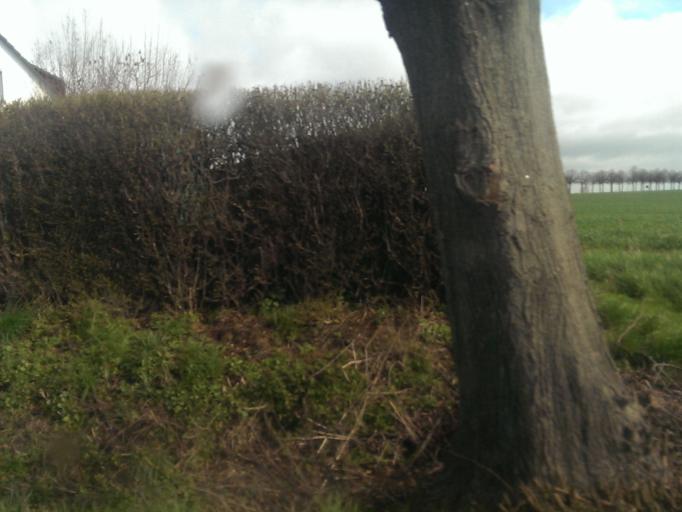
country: DE
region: Lower Saxony
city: Schellerten
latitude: 52.1711
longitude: 10.0421
